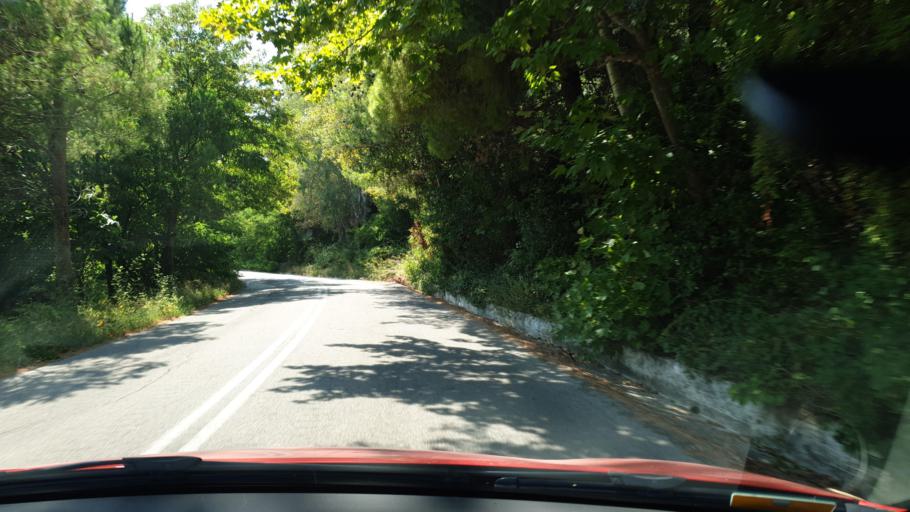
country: GR
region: Central Greece
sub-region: Nomos Evvoias
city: Kymi
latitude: 38.6275
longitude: 24.0999
